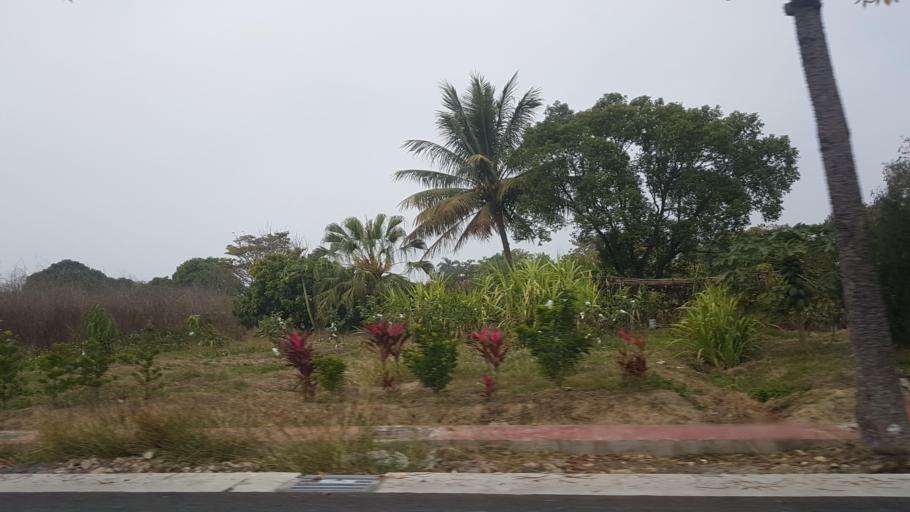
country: TW
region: Taiwan
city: Xinying
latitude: 23.3103
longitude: 120.2961
